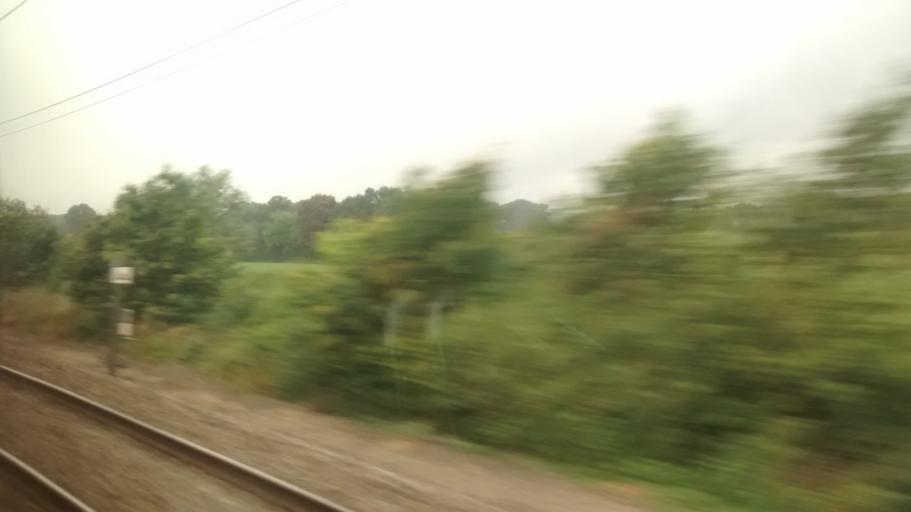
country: FR
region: Pays de la Loire
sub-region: Departement de la Sarthe
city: Vibraye
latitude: 48.0823
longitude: 0.7900
